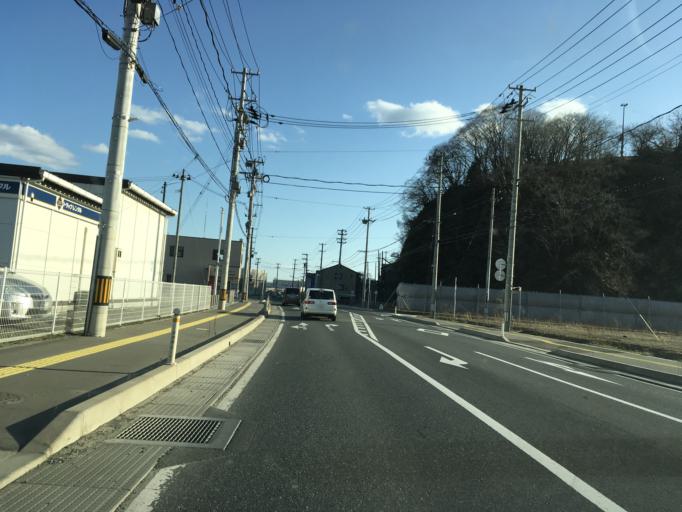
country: JP
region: Iwate
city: Ofunato
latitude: 38.9115
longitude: 141.5802
